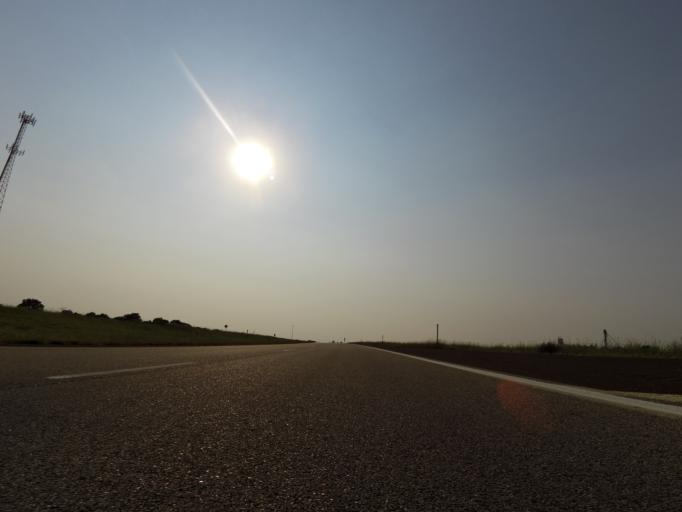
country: US
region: Kansas
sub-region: Reno County
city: Haven
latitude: 37.9359
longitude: -97.8633
